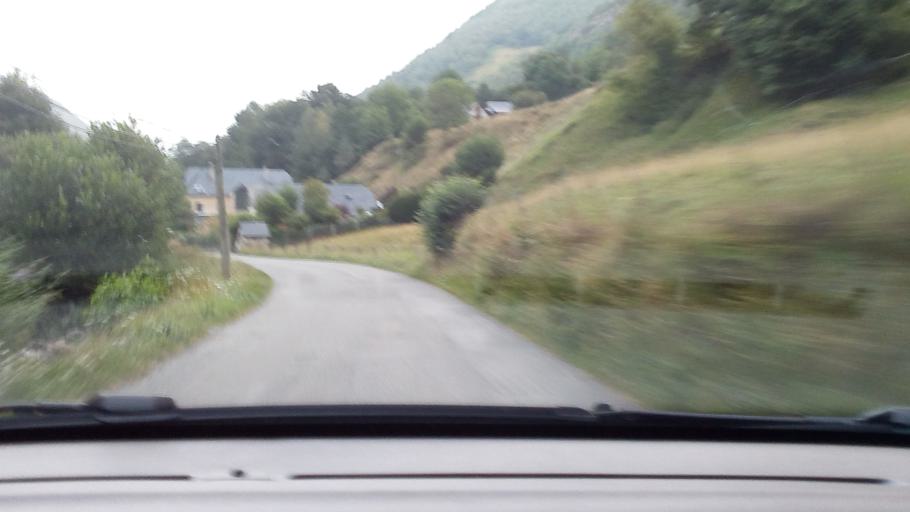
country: FR
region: Midi-Pyrenees
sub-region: Departement des Hautes-Pyrenees
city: Cauterets
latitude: 42.9280
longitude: -0.1810
